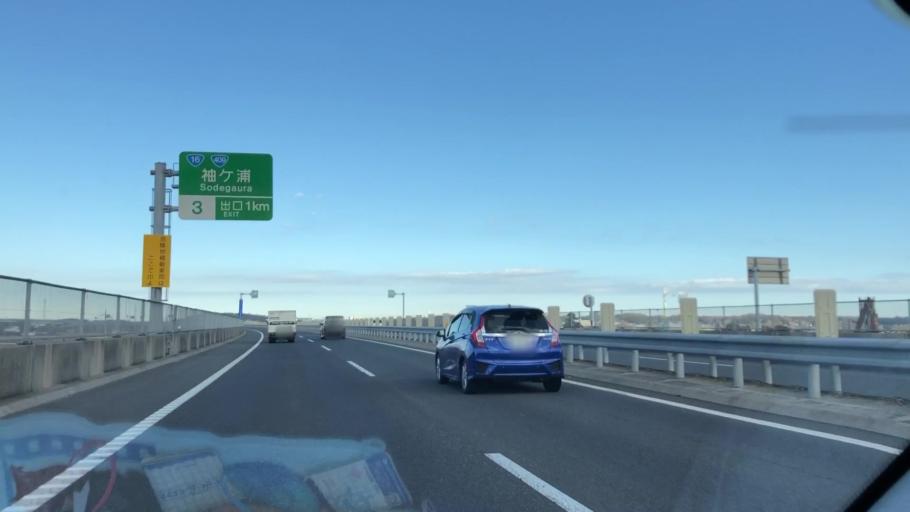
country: JP
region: Chiba
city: Kisarazu
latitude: 35.4015
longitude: 139.9665
